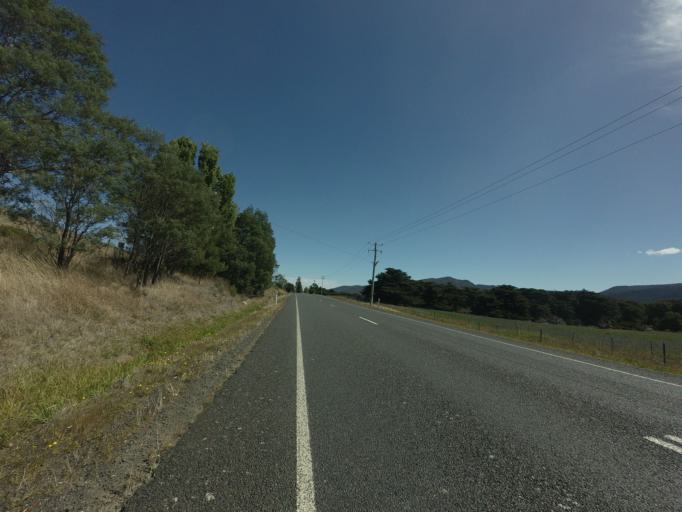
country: AU
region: Tasmania
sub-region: Break O'Day
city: St Helens
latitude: -41.7204
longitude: 147.8302
